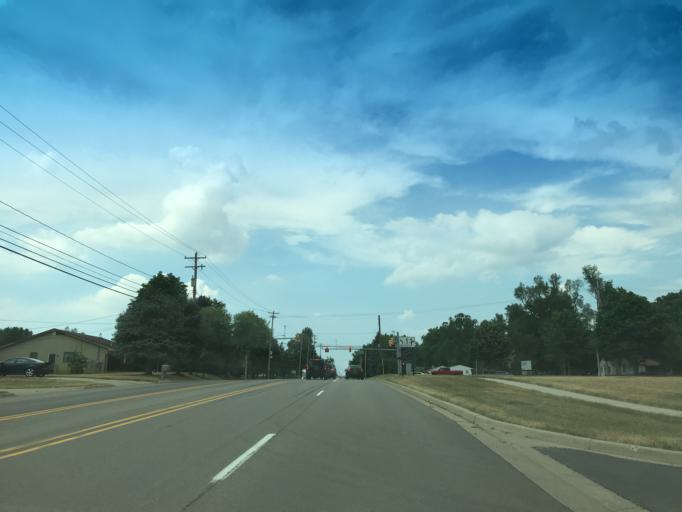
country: US
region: Michigan
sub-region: Eaton County
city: Waverly
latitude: 42.7255
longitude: -84.6620
